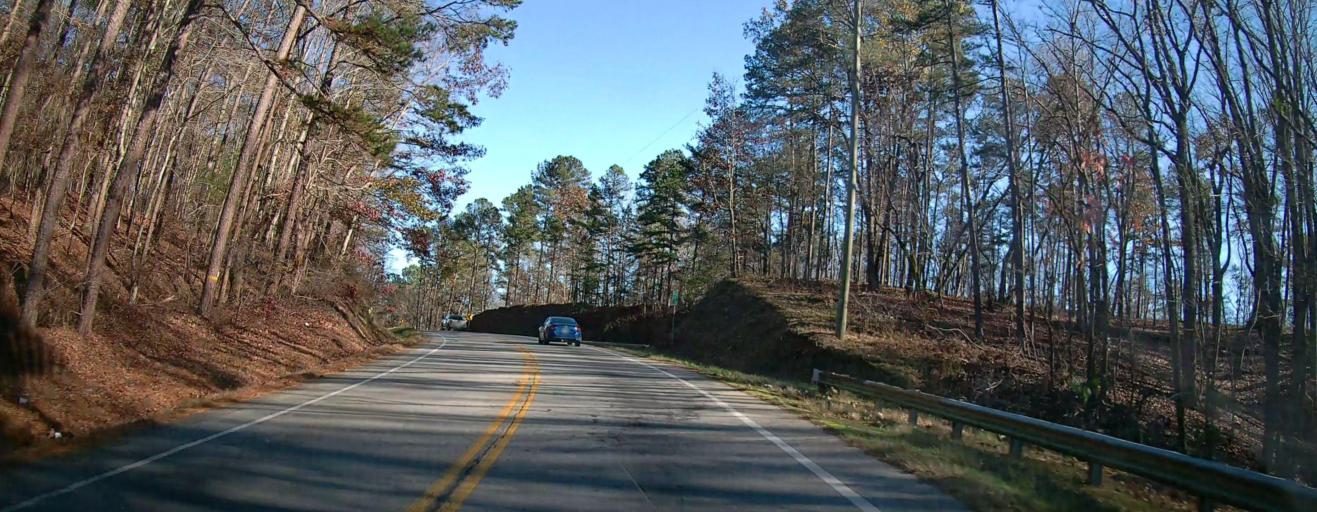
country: US
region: Georgia
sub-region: Hall County
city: Lula
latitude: 34.4058
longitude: -83.7088
